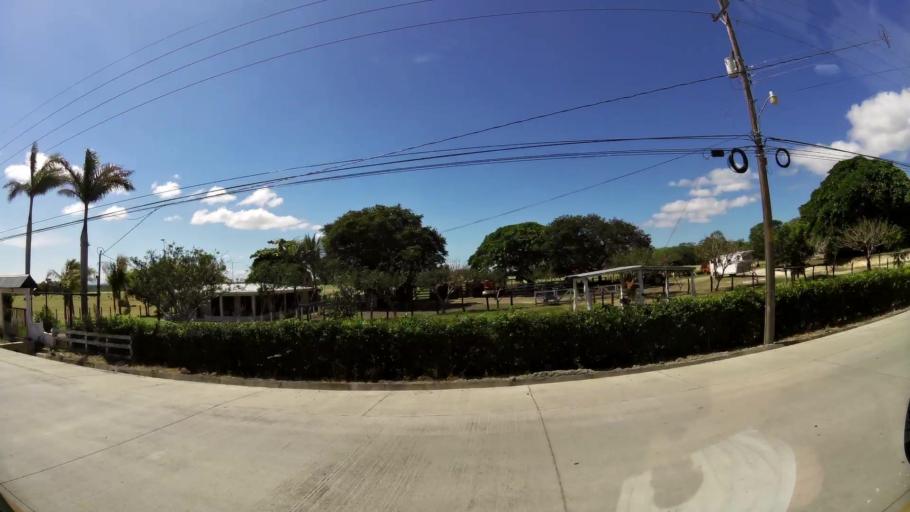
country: CR
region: Guanacaste
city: Bagaces
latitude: 10.5058
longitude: -85.2331
